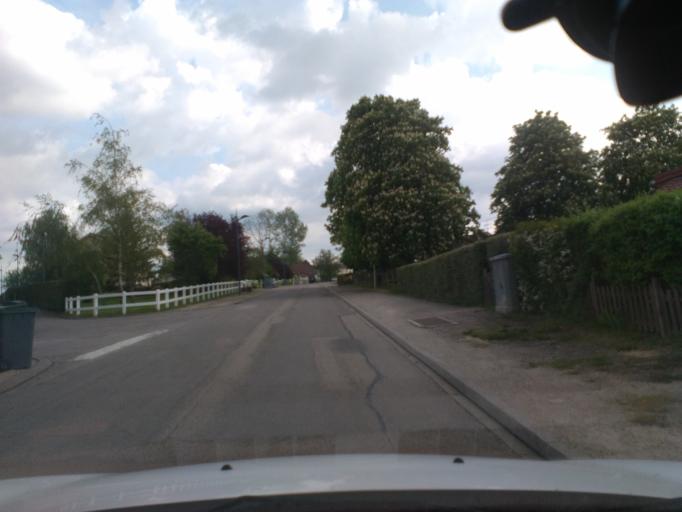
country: FR
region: Lorraine
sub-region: Departement des Vosges
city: Mirecourt
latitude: 48.3214
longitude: 6.1478
